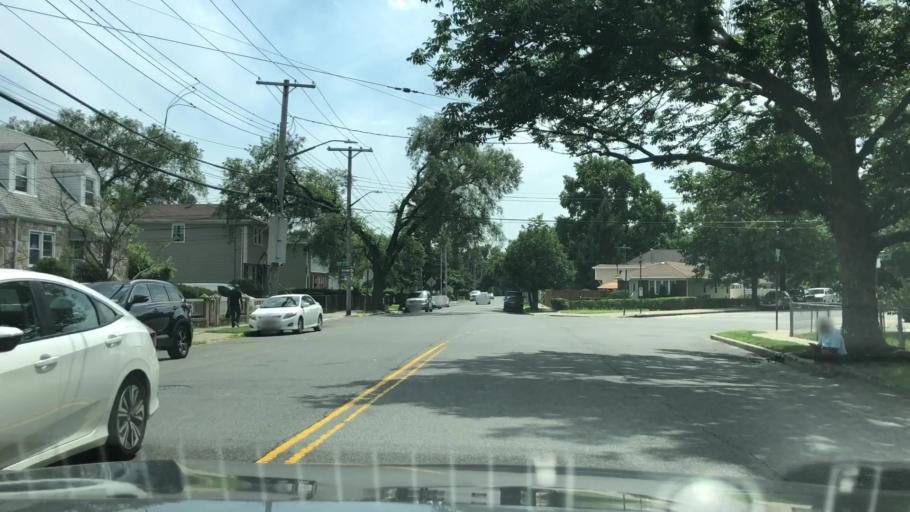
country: US
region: New York
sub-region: Queens County
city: Jamaica
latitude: 40.6970
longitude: -73.7760
